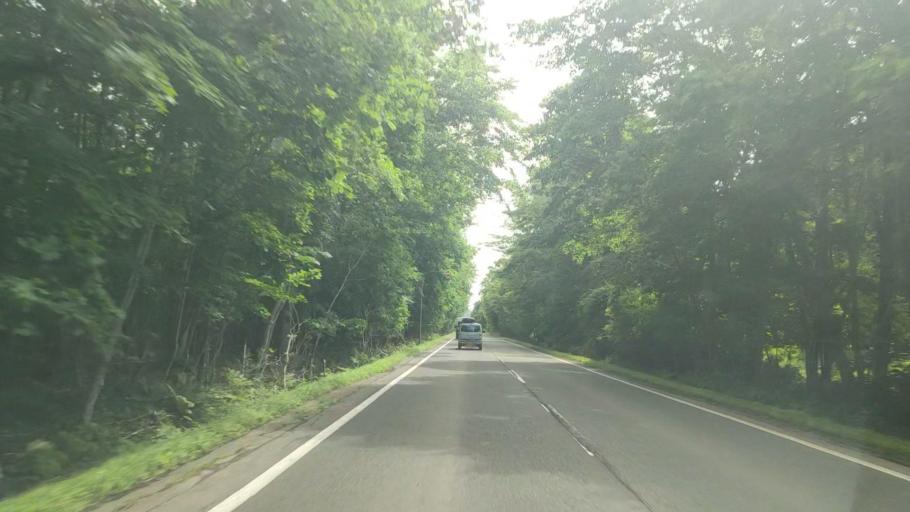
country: JP
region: Hokkaido
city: Tomakomai
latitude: 42.7738
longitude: 141.4405
